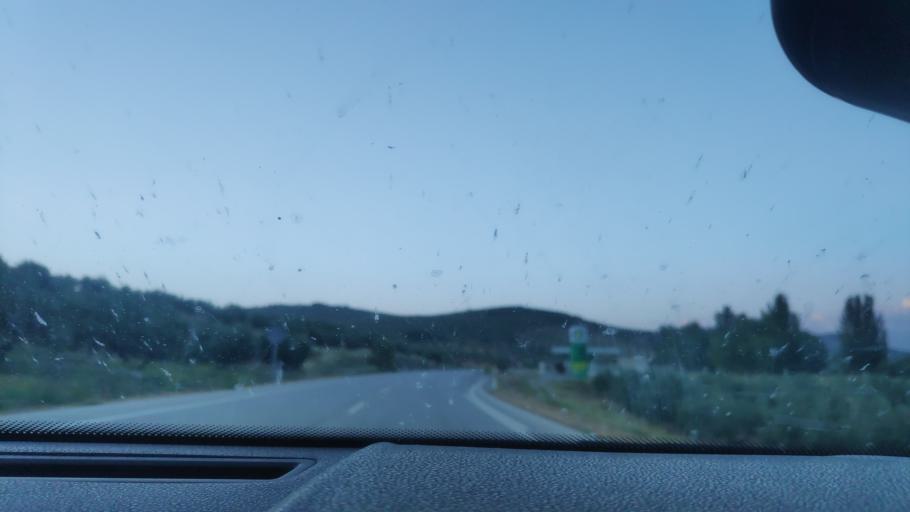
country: ES
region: Andalusia
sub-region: Provincia de Granada
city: Benalua de las Villas
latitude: 37.4433
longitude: -3.6515
